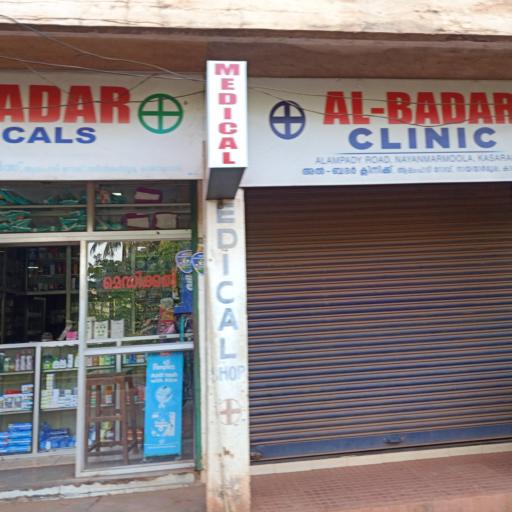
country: IN
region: Kerala
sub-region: Kasaragod District
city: Kasaragod
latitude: 12.5157
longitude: 75.0232
